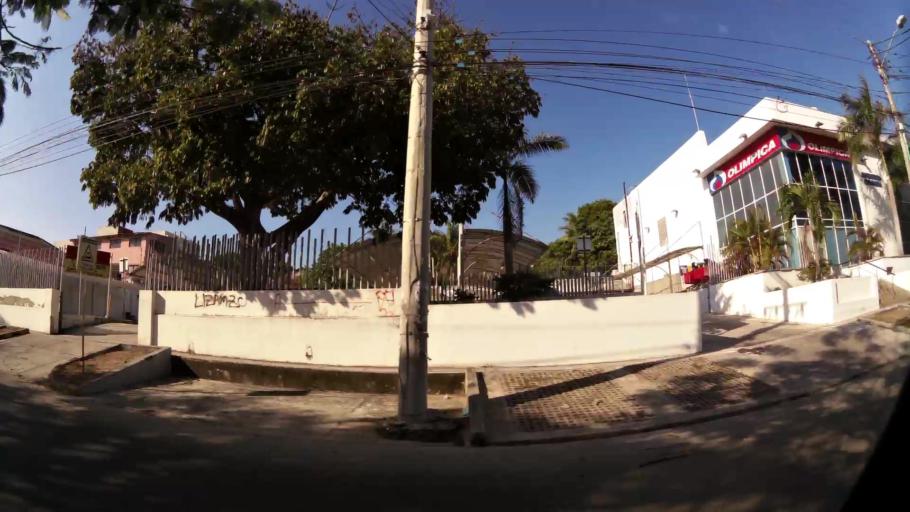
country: CO
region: Atlantico
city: Barranquilla
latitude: 11.0020
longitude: -74.7966
